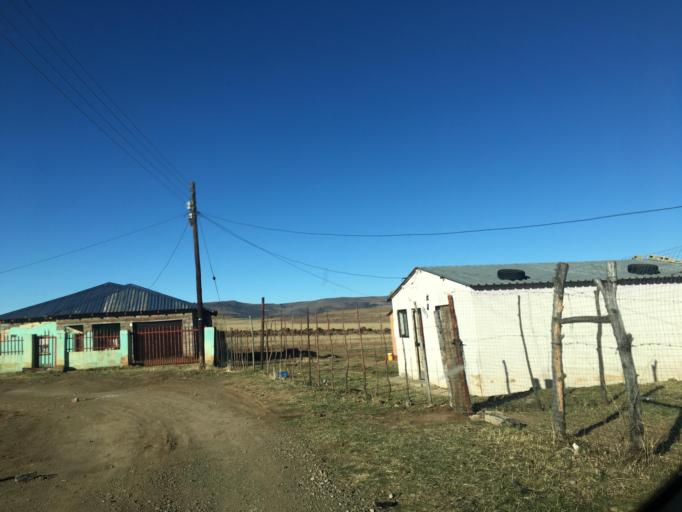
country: ZA
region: Eastern Cape
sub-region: Chris Hani District Municipality
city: Cala
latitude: -31.5413
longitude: 27.6774
